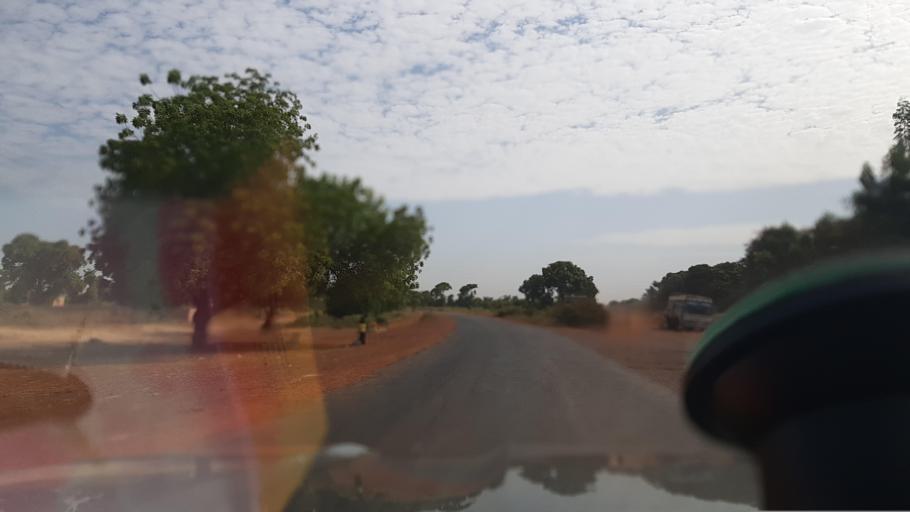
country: ML
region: Segou
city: Segou
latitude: 13.4997
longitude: -6.1534
